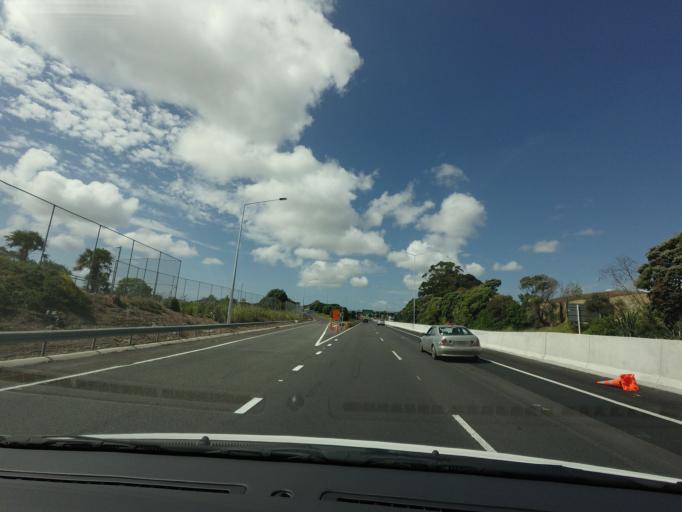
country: NZ
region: Auckland
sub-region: Auckland
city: Mangere
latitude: -36.9678
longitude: 174.7944
